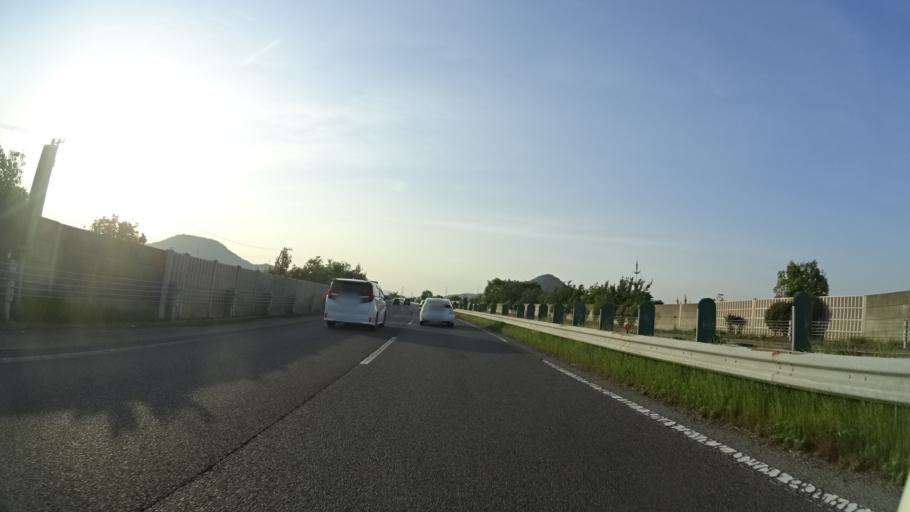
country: JP
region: Kagawa
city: Sakaidecho
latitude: 34.2894
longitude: 133.8506
